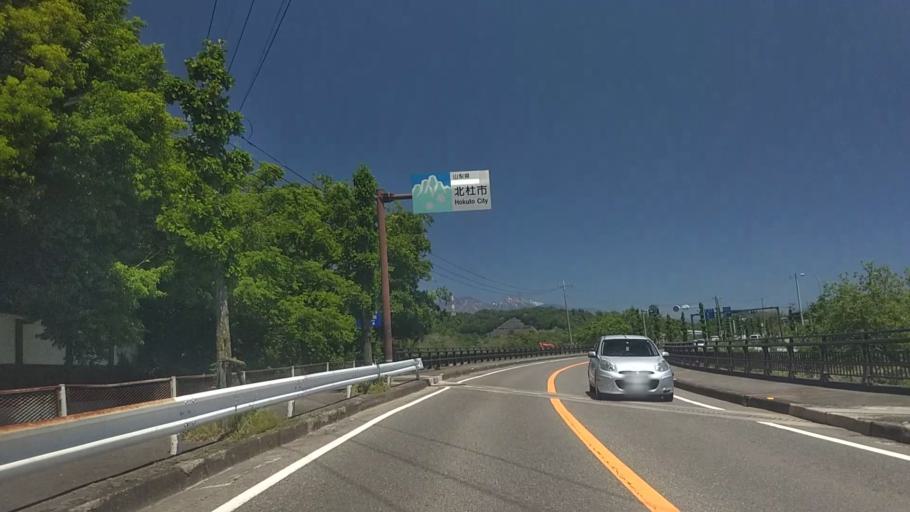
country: JP
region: Yamanashi
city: Nirasaki
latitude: 35.7729
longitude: 138.4190
